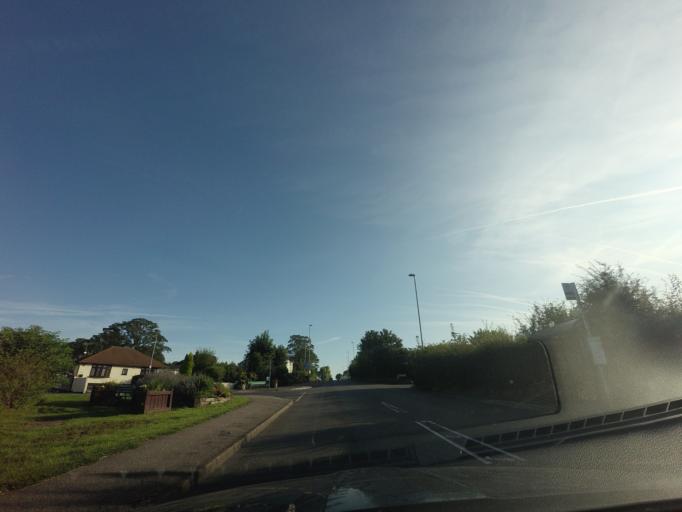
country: GB
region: England
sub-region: Derbyshire
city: Pinxton
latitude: 53.0491
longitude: -1.2951
